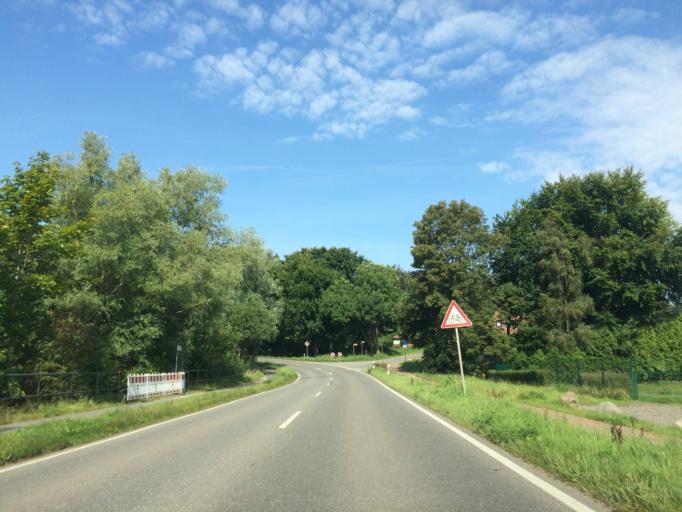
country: DE
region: Schleswig-Holstein
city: Preetz
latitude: 54.2447
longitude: 10.2693
